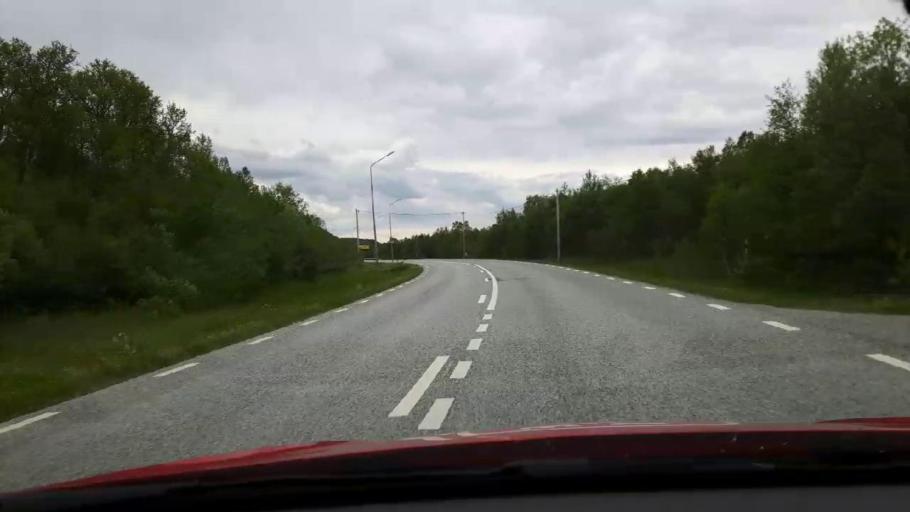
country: NO
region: Sor-Trondelag
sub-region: Tydal
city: Aas
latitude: 62.5833
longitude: 12.2025
